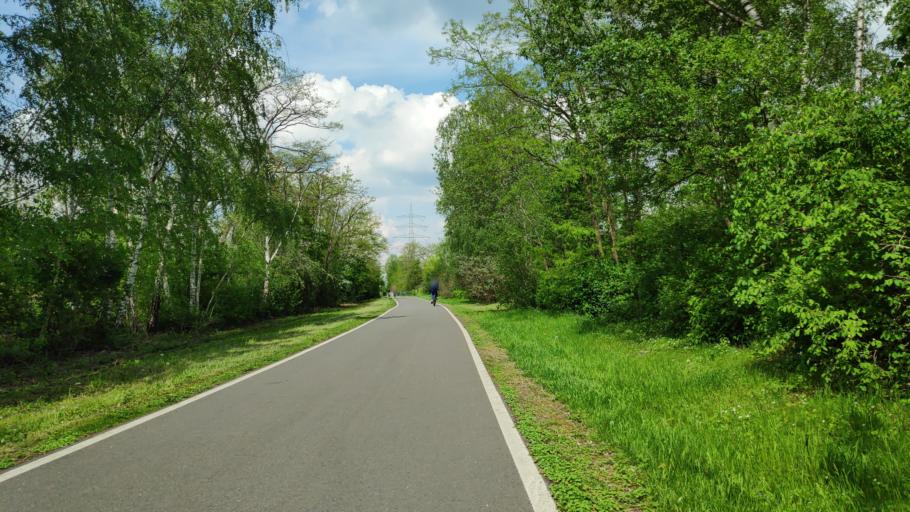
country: DE
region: North Rhine-Westphalia
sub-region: Regierungsbezirk Munster
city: Gelsenkirchen
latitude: 51.5220
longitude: 7.1395
